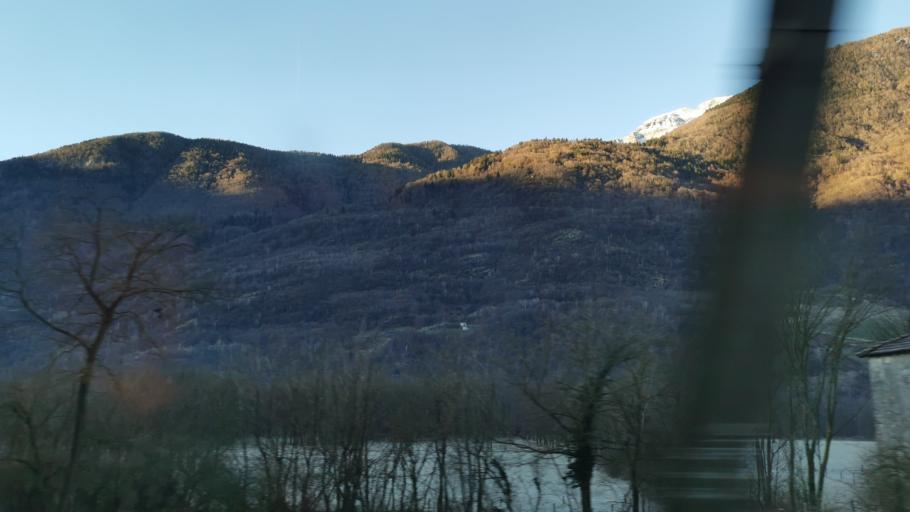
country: CH
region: Ticino
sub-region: Riviera District
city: Claro
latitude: 46.2474
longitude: 9.0200
